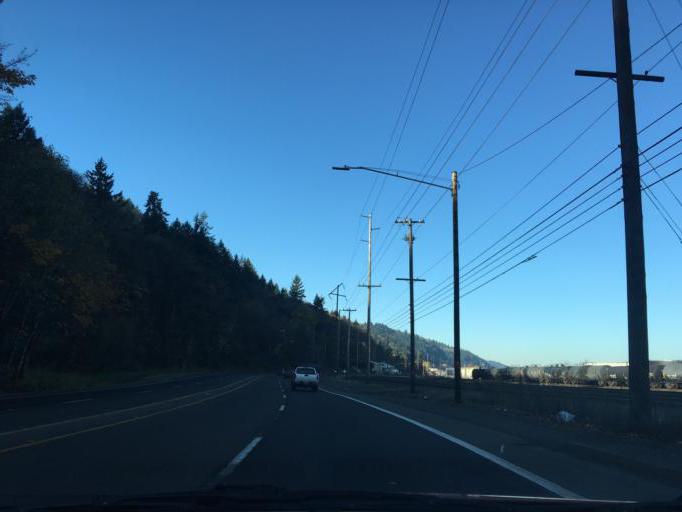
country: US
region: Oregon
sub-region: Washington County
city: West Haven
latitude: 45.5568
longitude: -122.7359
